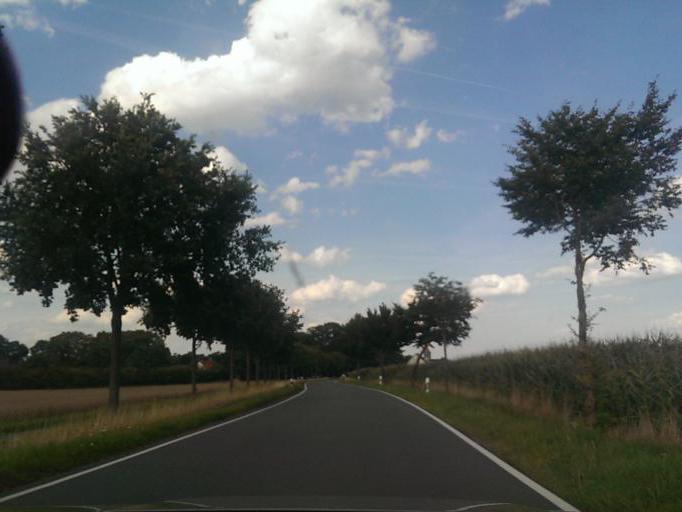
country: DE
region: North Rhine-Westphalia
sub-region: Regierungsbezirk Detmold
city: Delbruck
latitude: 51.7410
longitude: 8.5852
